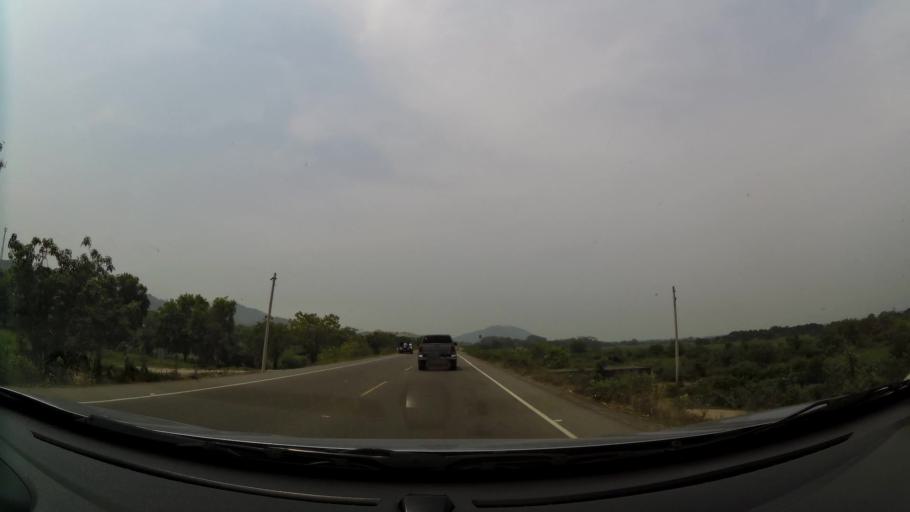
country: HN
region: Cortes
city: Potrerillos
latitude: 15.2292
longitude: -87.9596
